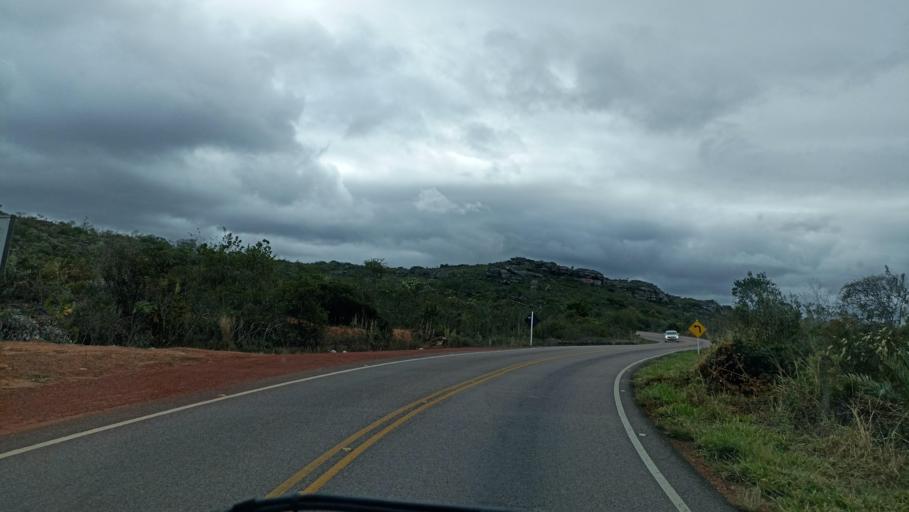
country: BR
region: Bahia
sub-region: Andarai
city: Vera Cruz
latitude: -12.9925
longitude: -41.3544
